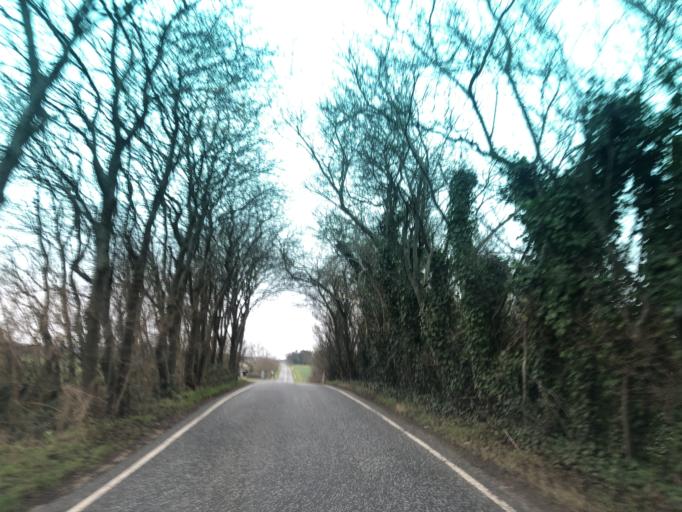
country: DK
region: Capital Region
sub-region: Allerod Kommune
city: Lynge
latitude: 55.8481
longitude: 12.2484
